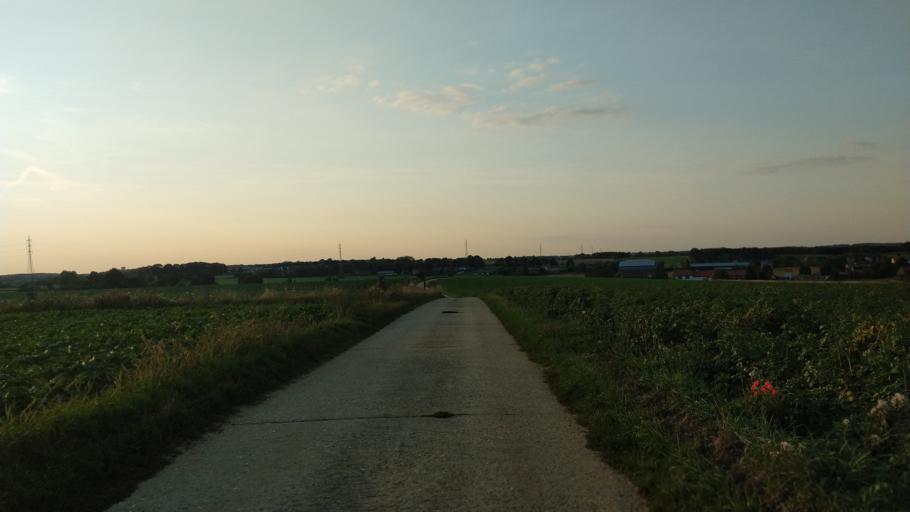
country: BE
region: Flanders
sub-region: Provincie Vlaams-Brabant
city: Lubbeek
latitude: 50.8848
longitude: 4.8105
